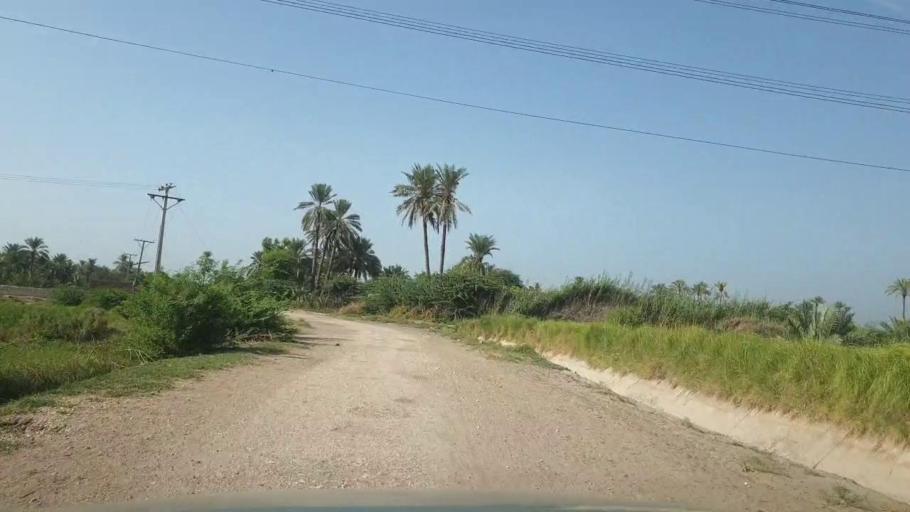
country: PK
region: Sindh
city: Rohri
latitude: 27.6617
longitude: 68.8837
